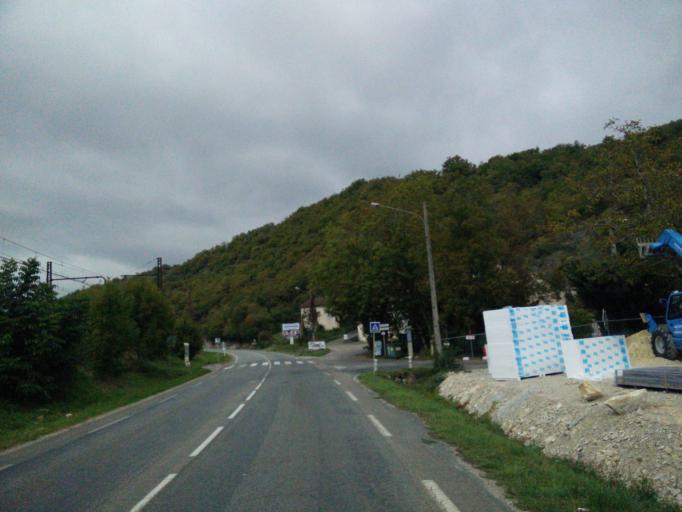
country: FR
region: Midi-Pyrenees
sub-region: Departement du Lot
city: Pradines
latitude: 44.4761
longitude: 1.4275
